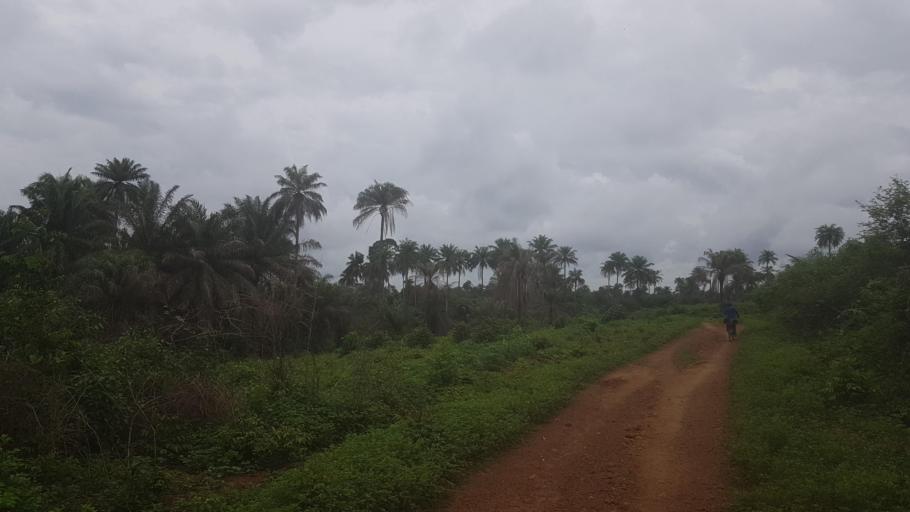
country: SL
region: Southern Province
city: Sumbuya
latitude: 7.5466
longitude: -12.1684
